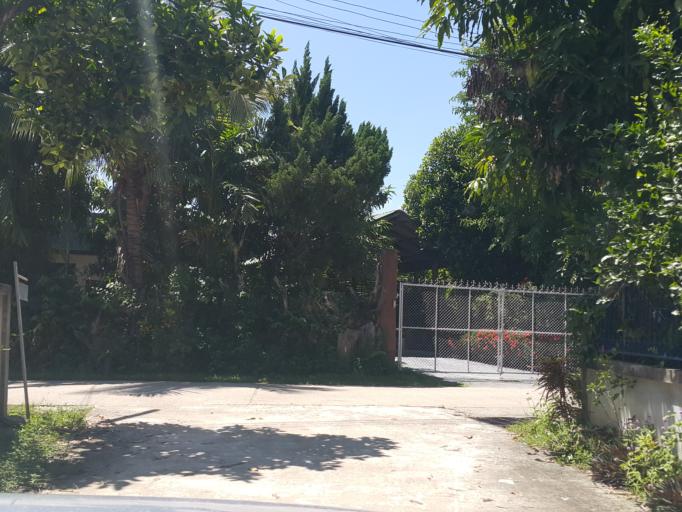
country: TH
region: Lamphun
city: Ban Thi
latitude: 18.6679
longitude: 99.1559
